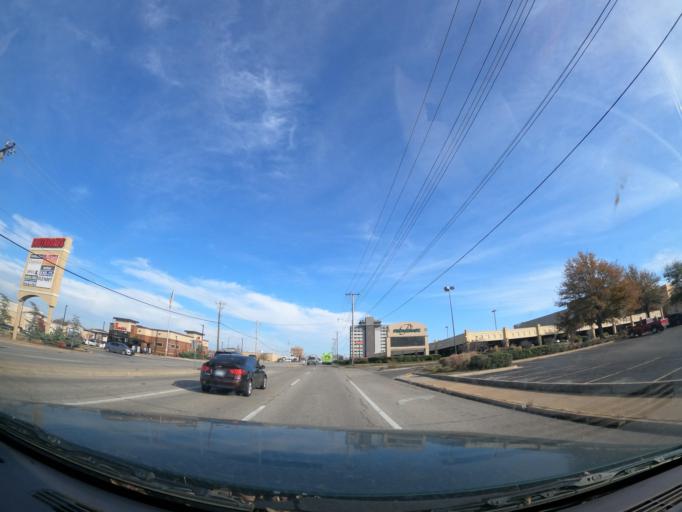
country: US
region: Oklahoma
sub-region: Tulsa County
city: Tulsa
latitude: 36.1044
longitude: -95.9206
